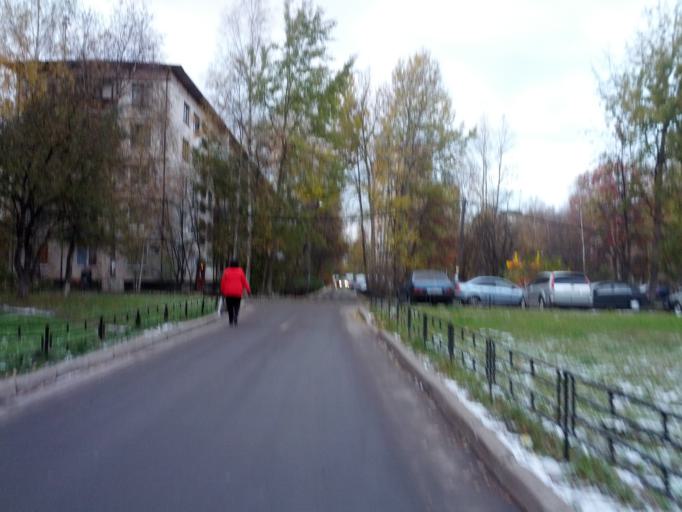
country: RU
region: St.-Petersburg
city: Obukhovo
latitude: 59.9007
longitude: 30.4784
